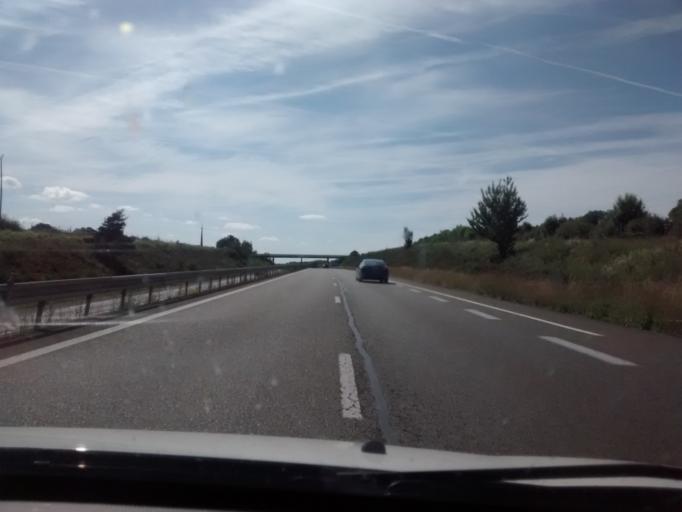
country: FR
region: Pays de la Loire
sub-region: Departement de la Mayenne
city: Vaiges
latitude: 48.0572
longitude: -0.4873
